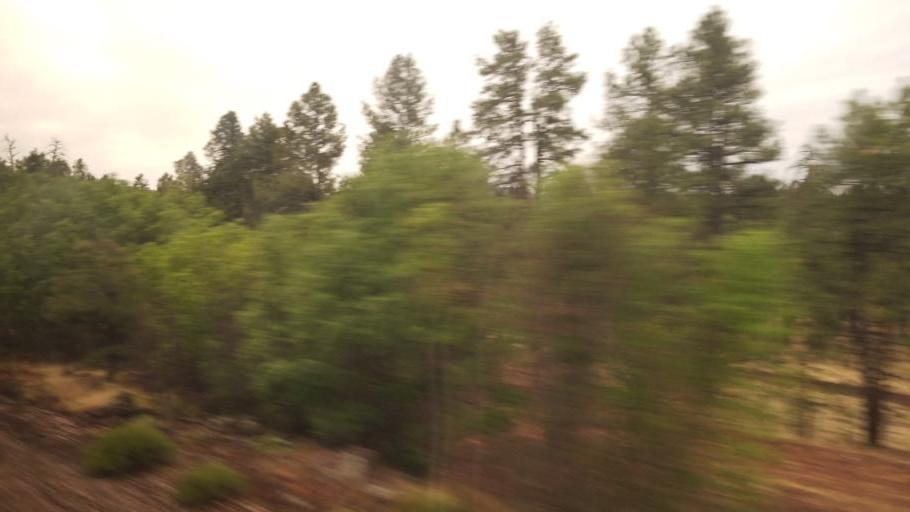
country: US
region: Arizona
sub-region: Coconino County
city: Parks
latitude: 35.2516
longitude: -111.9113
